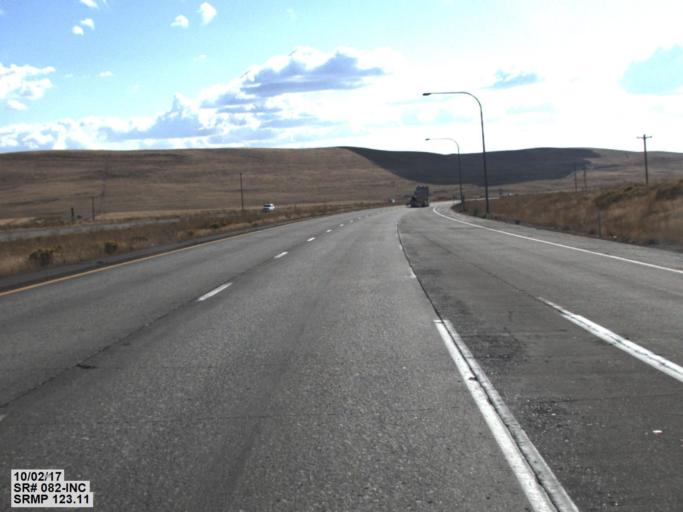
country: US
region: Oregon
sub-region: Umatilla County
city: Umatilla
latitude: 46.0201
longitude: -119.2258
